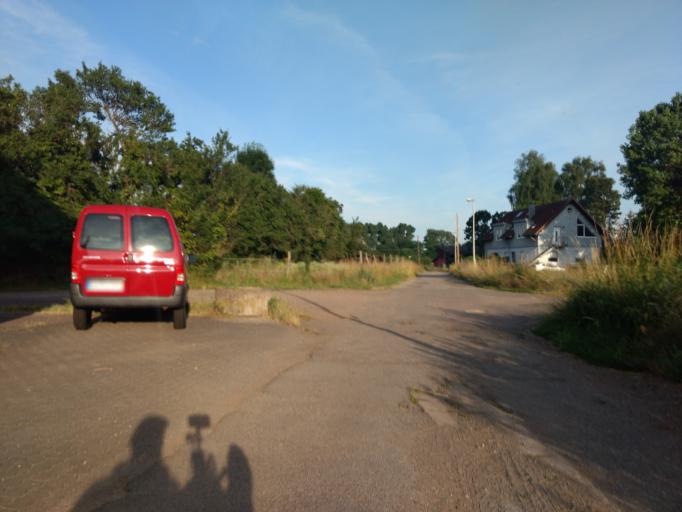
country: DE
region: Saarland
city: Wallerfangen
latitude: 49.3193
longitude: 6.7272
